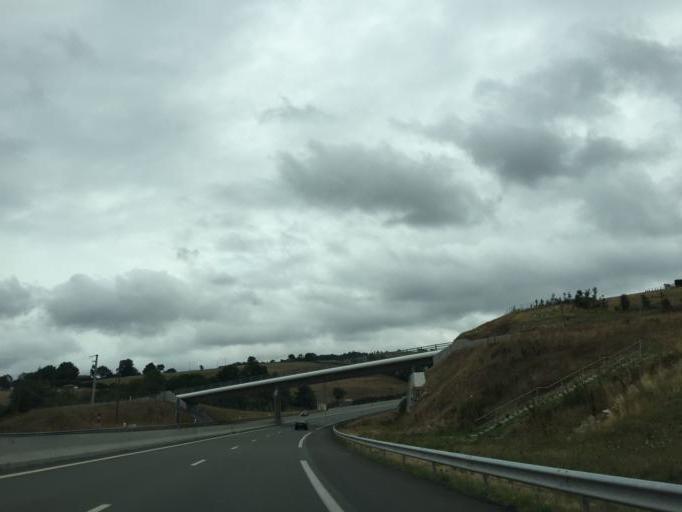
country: FR
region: Rhone-Alpes
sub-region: Departement de la Loire
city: Saint-Just-la-Pendue
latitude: 45.8627
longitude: 4.2354
